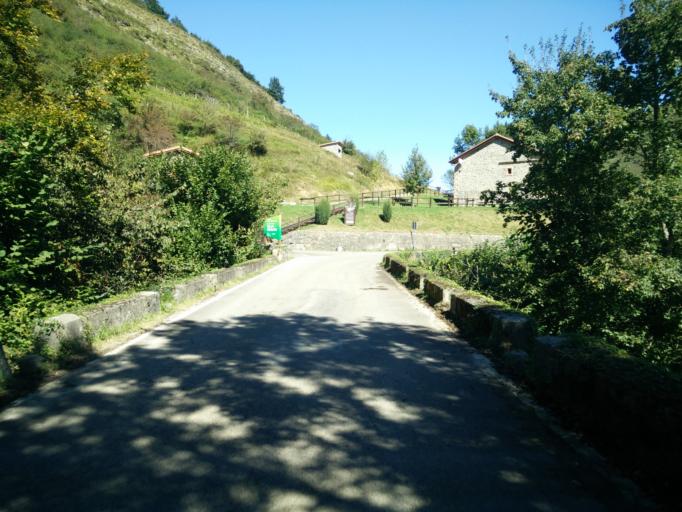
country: ES
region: Cantabria
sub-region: Provincia de Cantabria
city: Ruente
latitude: 43.1294
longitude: -4.2968
